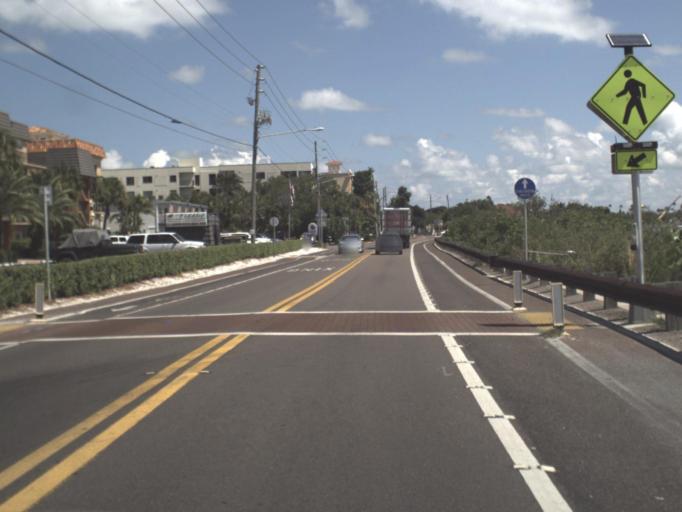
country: US
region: Florida
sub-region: Pinellas County
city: Indian Rocks Beach
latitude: 27.8757
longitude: -82.8503
